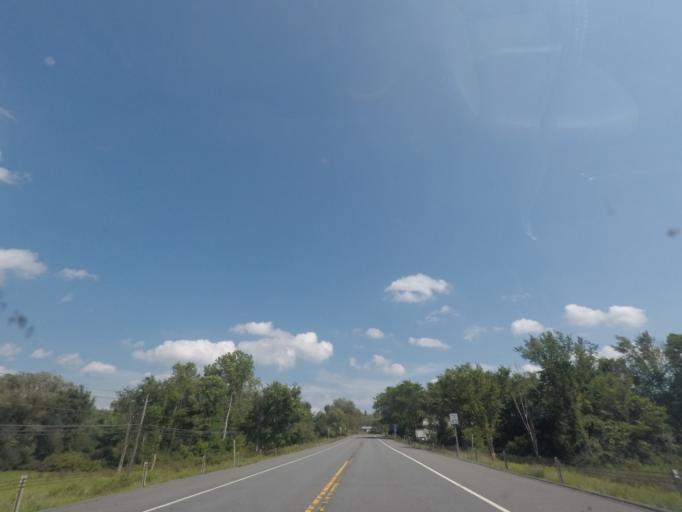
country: US
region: New York
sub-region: Rensselaer County
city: Hoosick Falls
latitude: 42.8457
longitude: -73.4613
